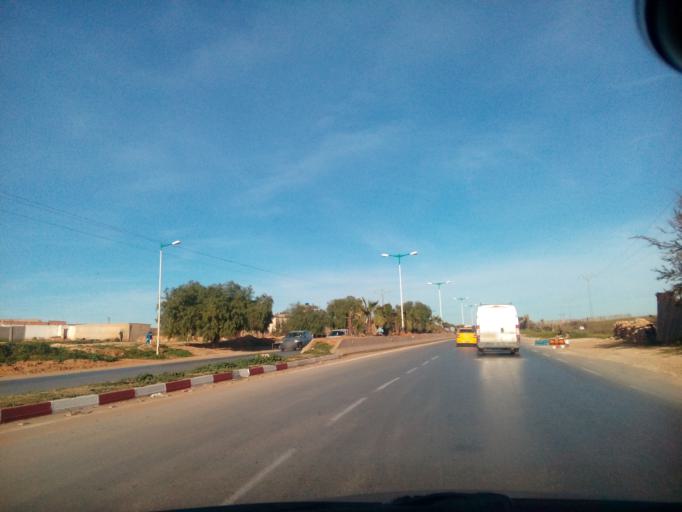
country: DZ
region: Mostaganem
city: Mostaganem
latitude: 35.8700
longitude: 0.1500
